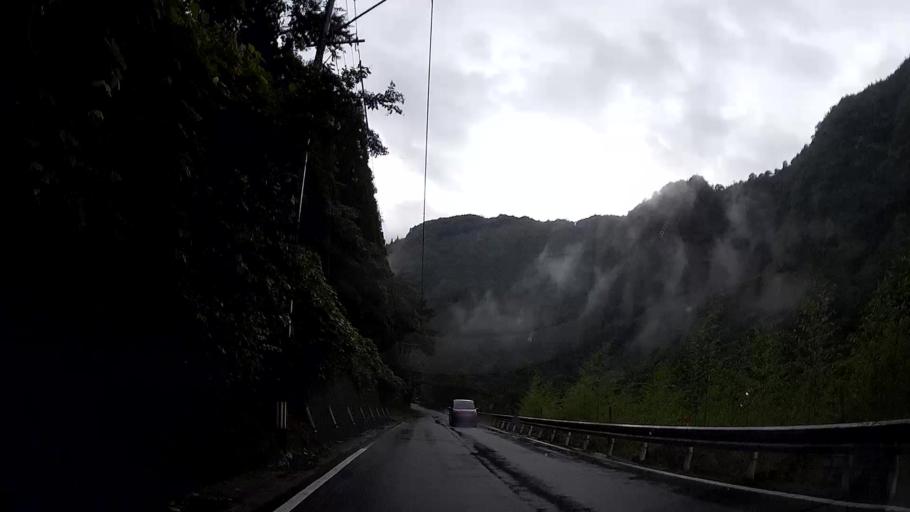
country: JP
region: Oita
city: Hita
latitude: 33.1792
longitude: 131.0125
